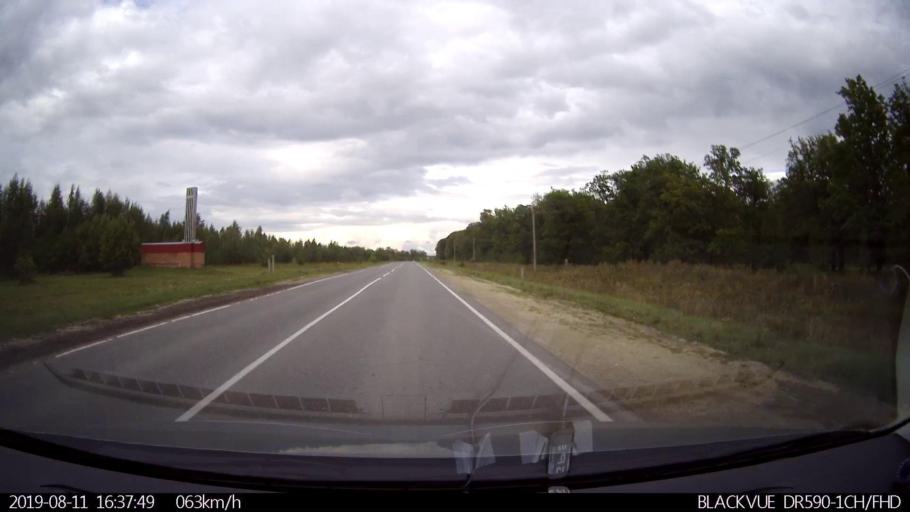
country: RU
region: Ulyanovsk
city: Mayna
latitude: 54.1305
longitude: 47.6173
